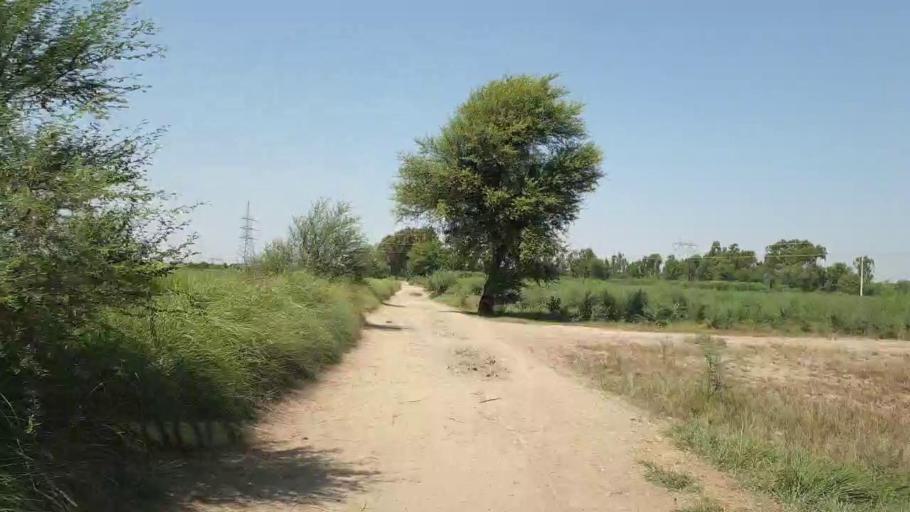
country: PK
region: Sindh
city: Hyderabad
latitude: 25.4757
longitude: 68.4163
